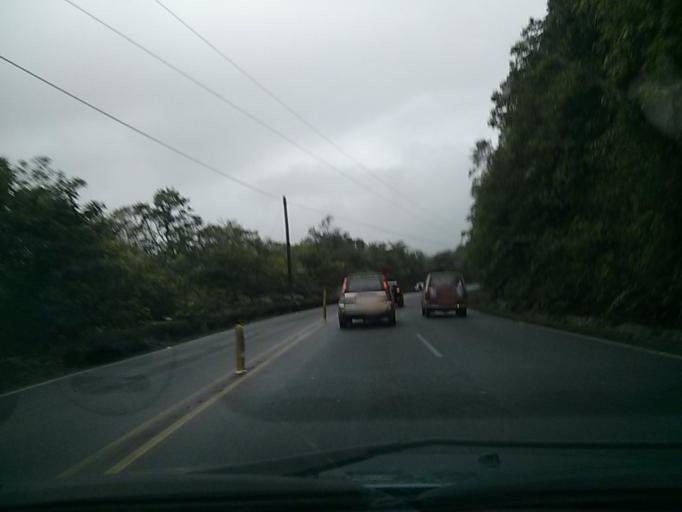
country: CR
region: Heredia
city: Angeles
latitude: 10.0559
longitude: -84.0070
